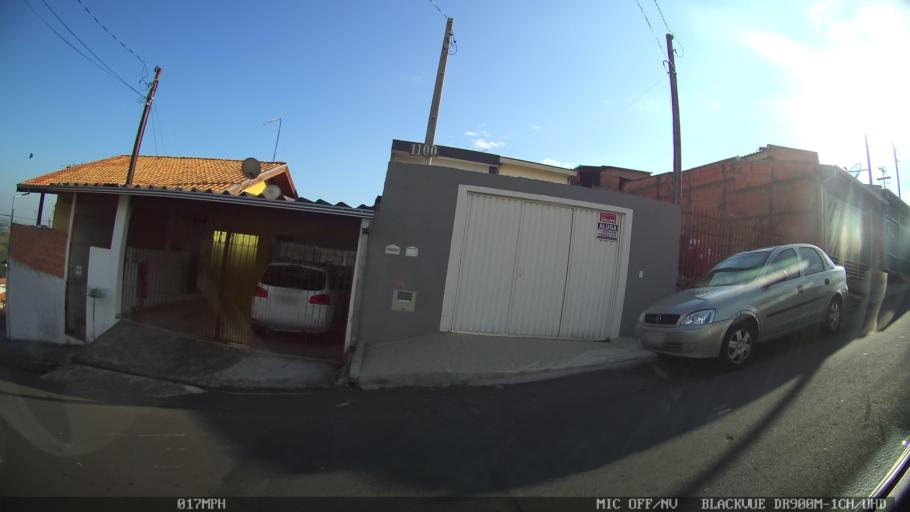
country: BR
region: Sao Paulo
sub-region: Americana
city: Americana
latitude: -22.7259
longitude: -47.3737
